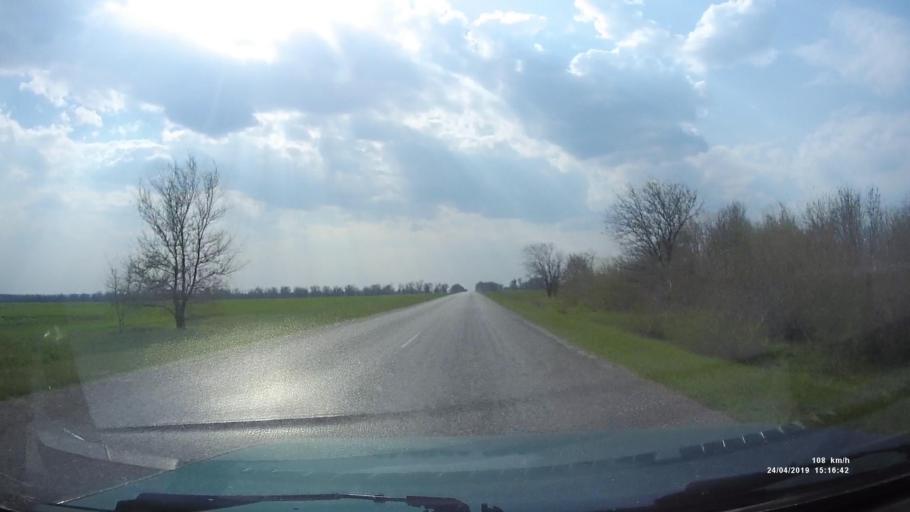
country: RU
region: Rostov
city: Remontnoye
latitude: 46.5466
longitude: 43.2041
